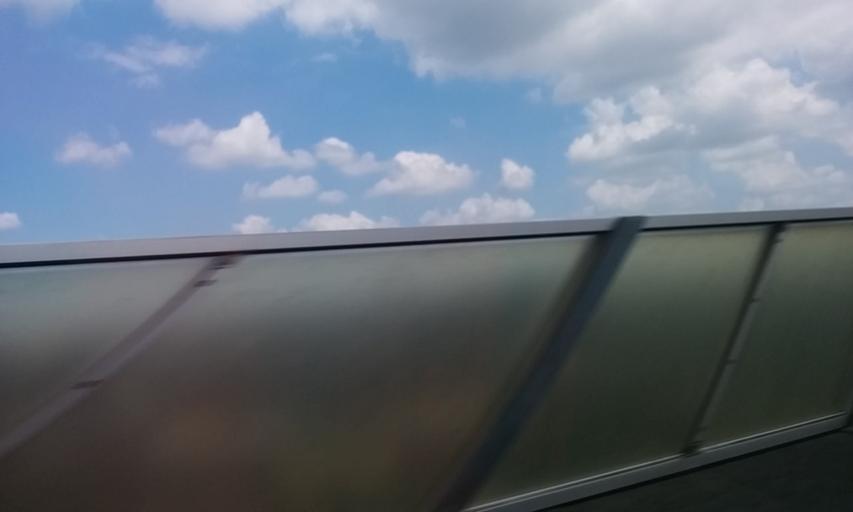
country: JP
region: Saitama
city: Ageoshimo
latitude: 35.9892
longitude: 139.6308
